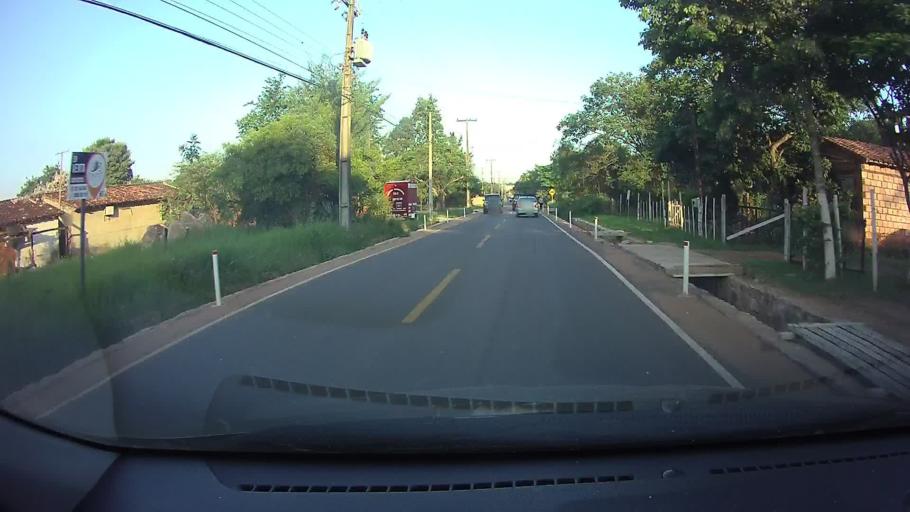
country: PY
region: Central
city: Limpio
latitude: -25.2514
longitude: -57.4954
